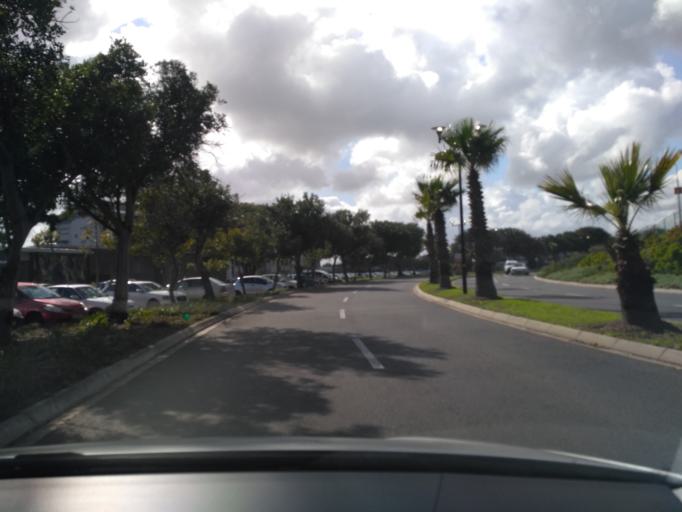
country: ZA
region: Western Cape
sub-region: City of Cape Town
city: Kraaifontein
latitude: -33.9342
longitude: 18.6227
